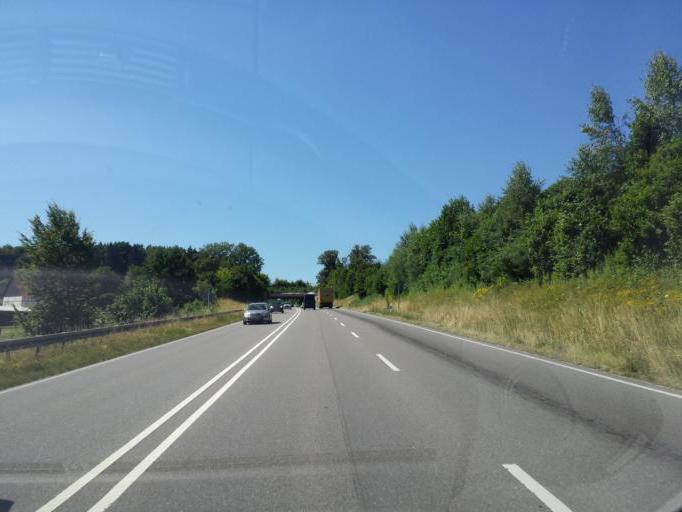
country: DE
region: Baden-Wuerttemberg
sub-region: Tuebingen Region
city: Owingen
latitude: 47.7974
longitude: 9.1395
